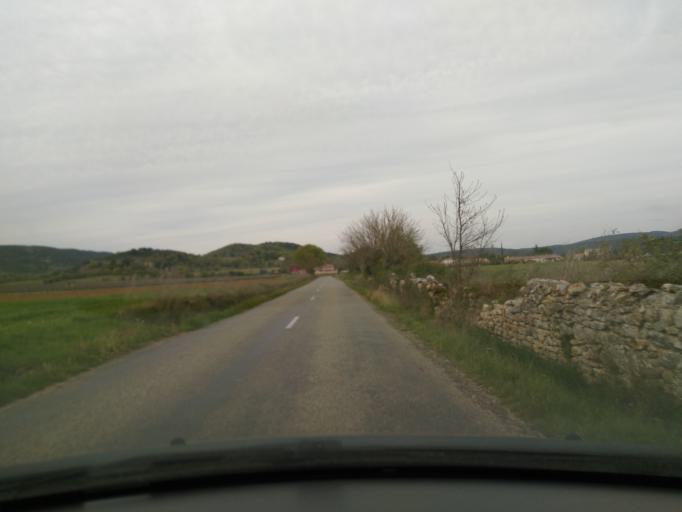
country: FR
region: Rhone-Alpes
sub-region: Departement de l'Ardeche
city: Ruoms
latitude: 44.4138
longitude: 4.4088
